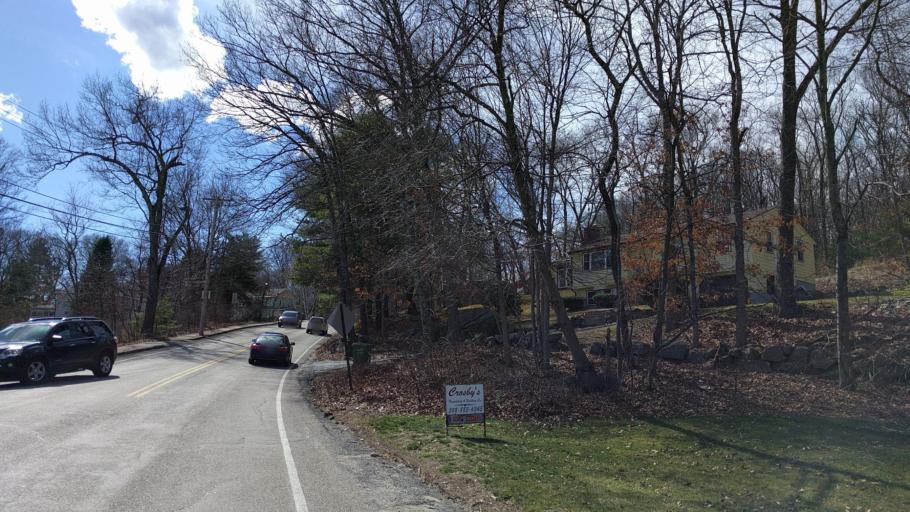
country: US
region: Massachusetts
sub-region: Worcester County
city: Uxbridge
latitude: 42.0972
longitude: -71.6240
